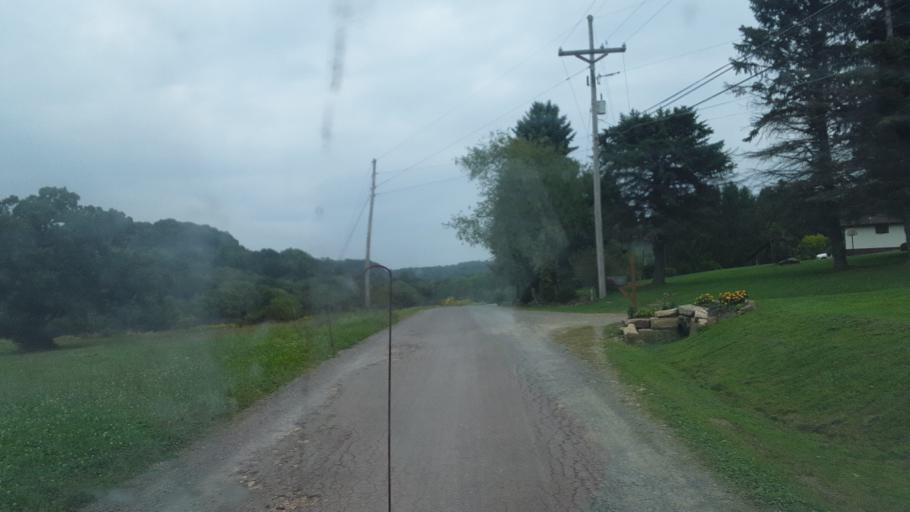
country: US
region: Pennsylvania
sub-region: Jefferson County
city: Punxsutawney
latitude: 40.9695
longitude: -79.1398
